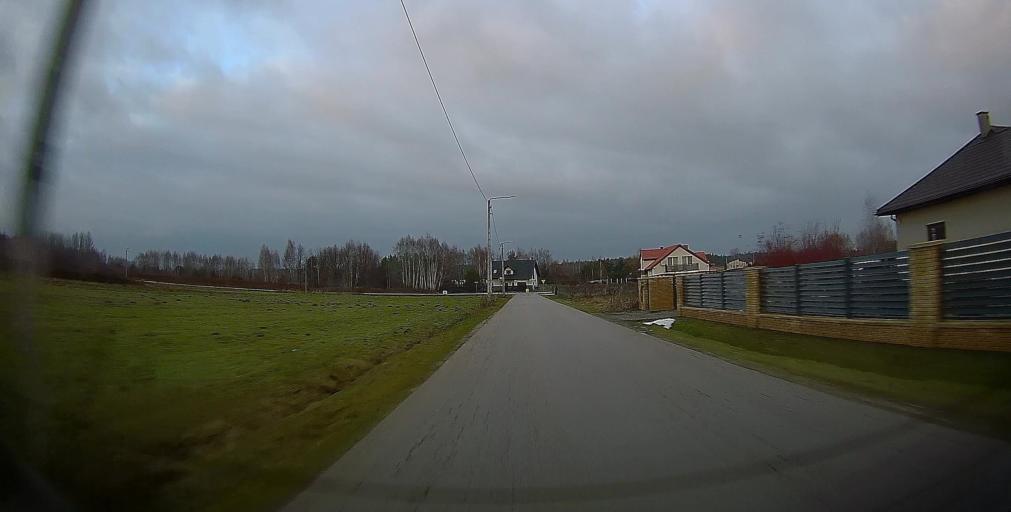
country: PL
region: Masovian Voivodeship
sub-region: Powiat radomski
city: Jedlinsk
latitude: 51.4591
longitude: 21.1233
